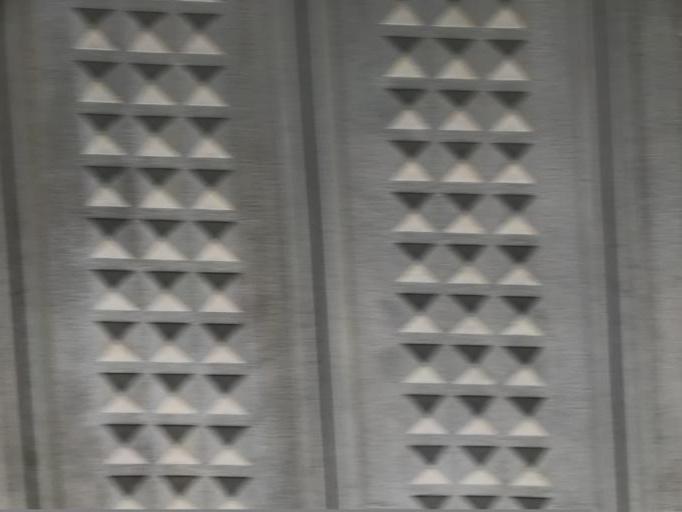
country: TR
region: Istanbul
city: Pendik
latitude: 40.8591
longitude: 29.2749
